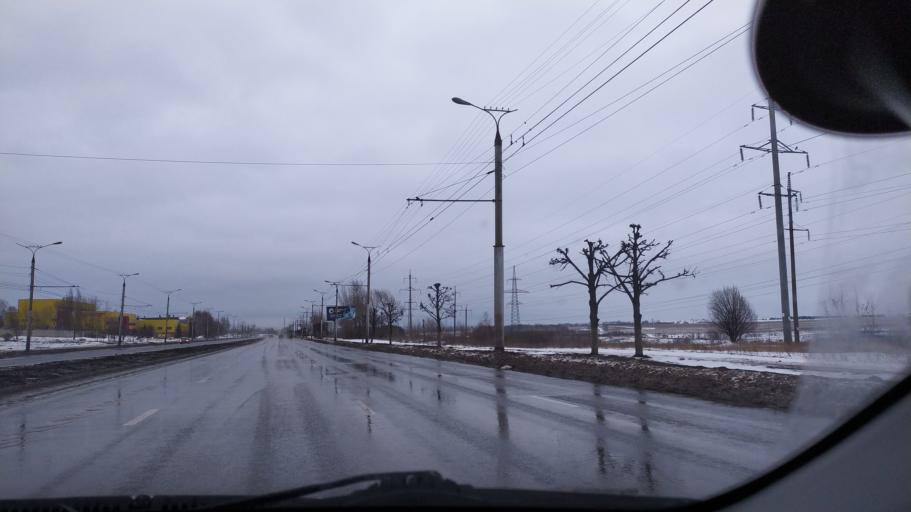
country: RU
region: Chuvashia
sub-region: Cheboksarskiy Rayon
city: Cheboksary
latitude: 56.1137
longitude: 47.3459
